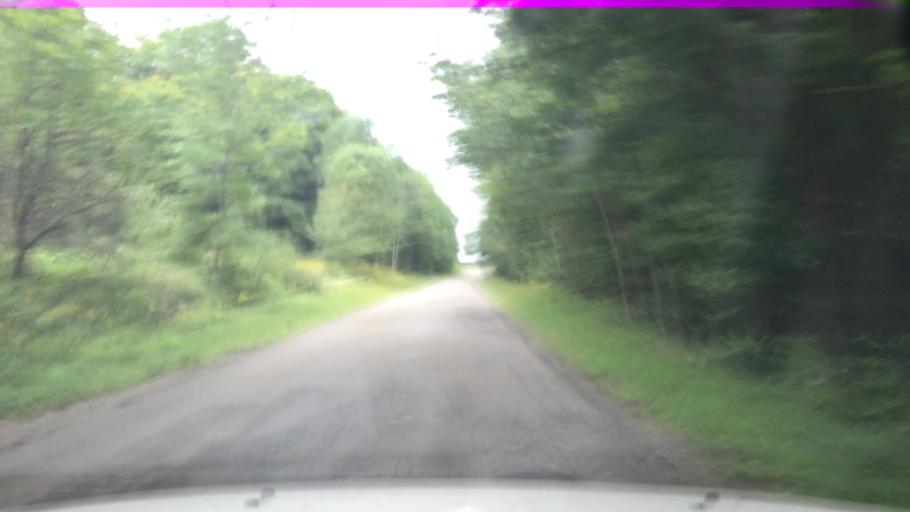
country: US
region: New York
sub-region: Cattaraugus County
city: Little Valley
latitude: 42.3265
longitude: -78.7244
